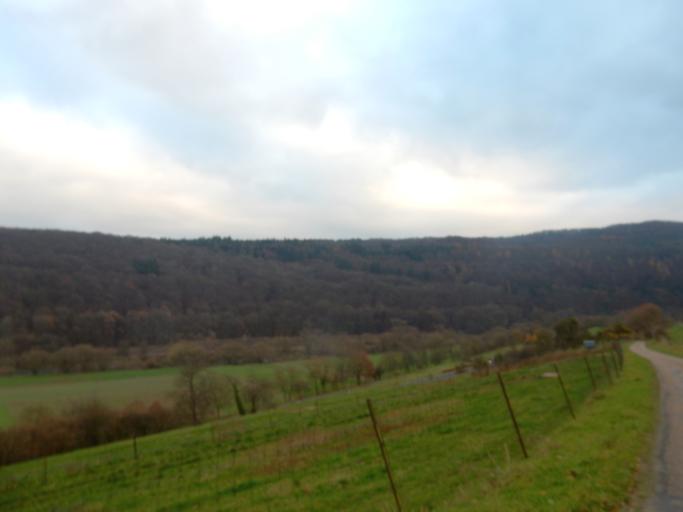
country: LU
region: Grevenmacher
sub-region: Canton d'Echternach
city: Rosport
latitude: 49.7677
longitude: 6.5125
